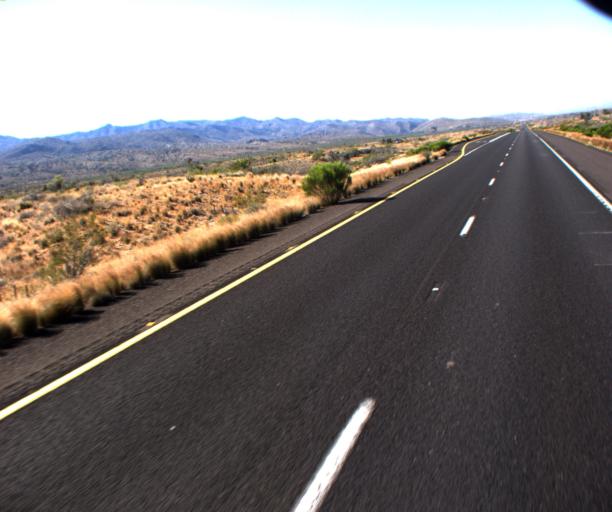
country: US
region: Arizona
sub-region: Mohave County
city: Kingman
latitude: 35.0701
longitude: -113.6658
